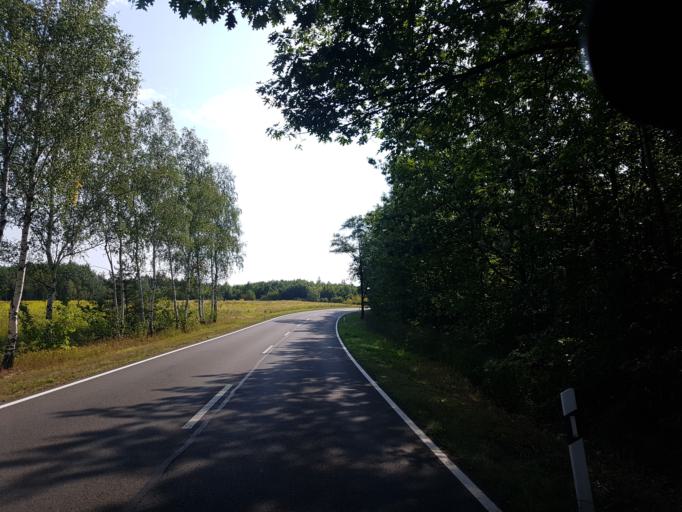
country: DE
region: Brandenburg
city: Lauchhammer
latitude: 51.5297
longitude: 13.7111
